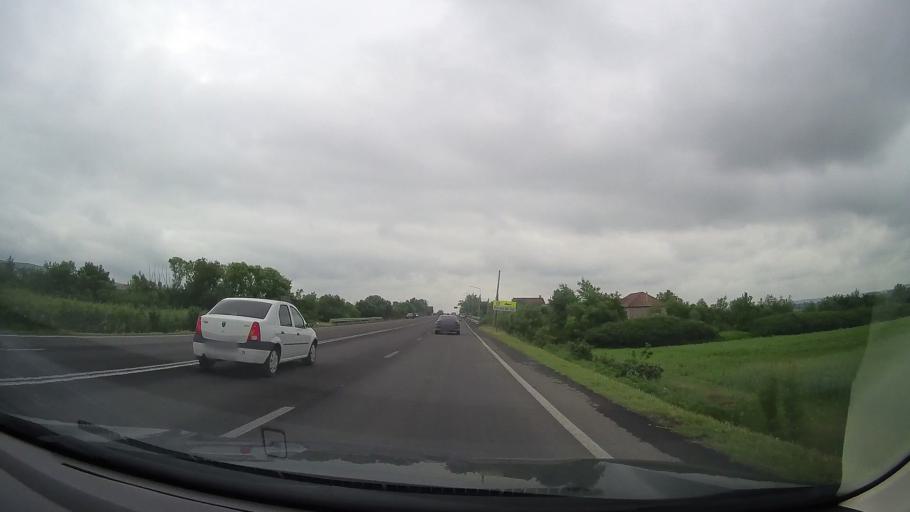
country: RO
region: Dolj
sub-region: Comuna Filiasi
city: Racarii de Sus
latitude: 44.5223
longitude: 23.5652
